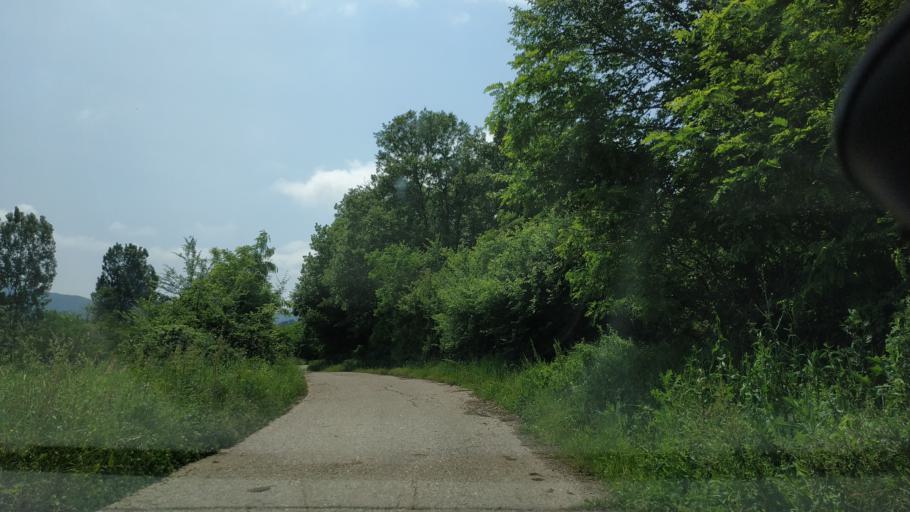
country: RS
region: Central Serbia
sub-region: Nisavski Okrug
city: Aleksinac
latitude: 43.4272
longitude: 21.7263
